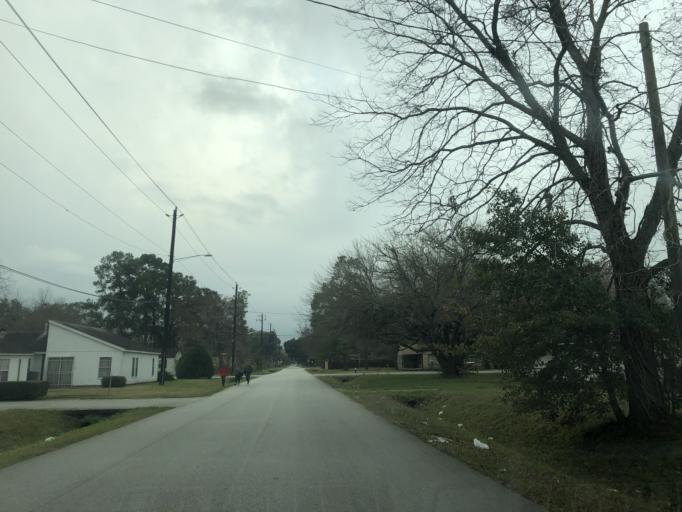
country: US
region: Texas
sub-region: Harris County
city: Jacinto City
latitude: 29.8335
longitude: -95.2938
